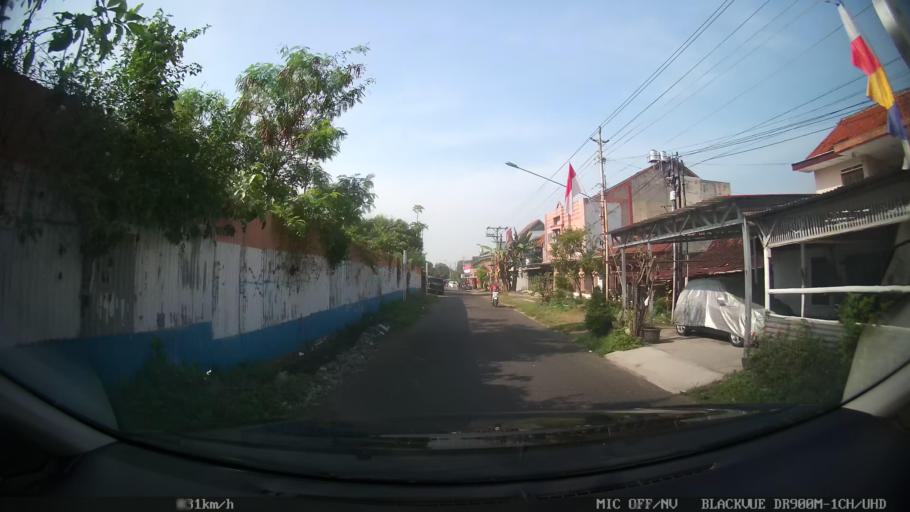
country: ID
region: Daerah Istimewa Yogyakarta
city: Yogyakarta
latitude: -7.7854
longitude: 110.3587
